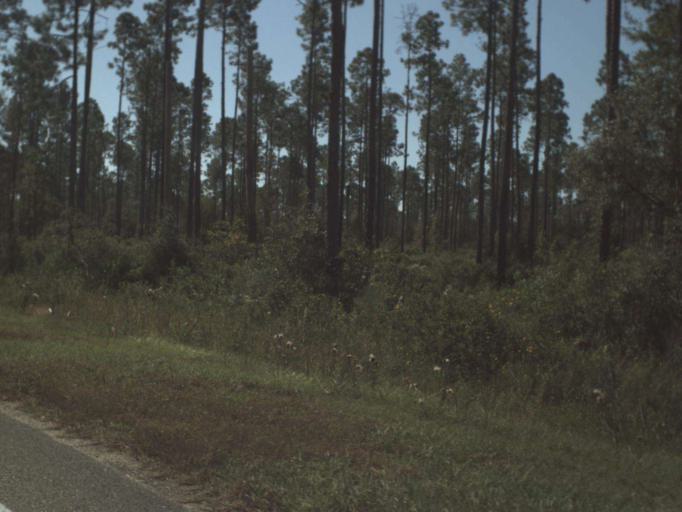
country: US
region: Florida
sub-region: Leon County
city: Woodville
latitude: 30.2148
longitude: -84.1981
